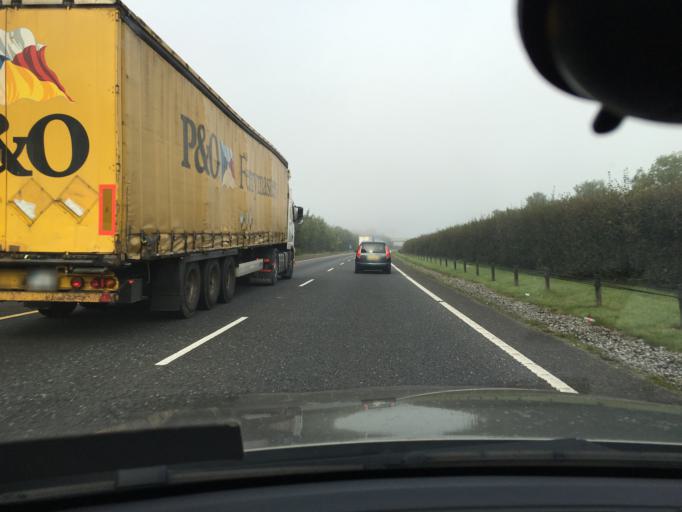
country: IE
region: Leinster
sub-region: Kildare
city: Kilcock
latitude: 53.3824
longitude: -6.6579
